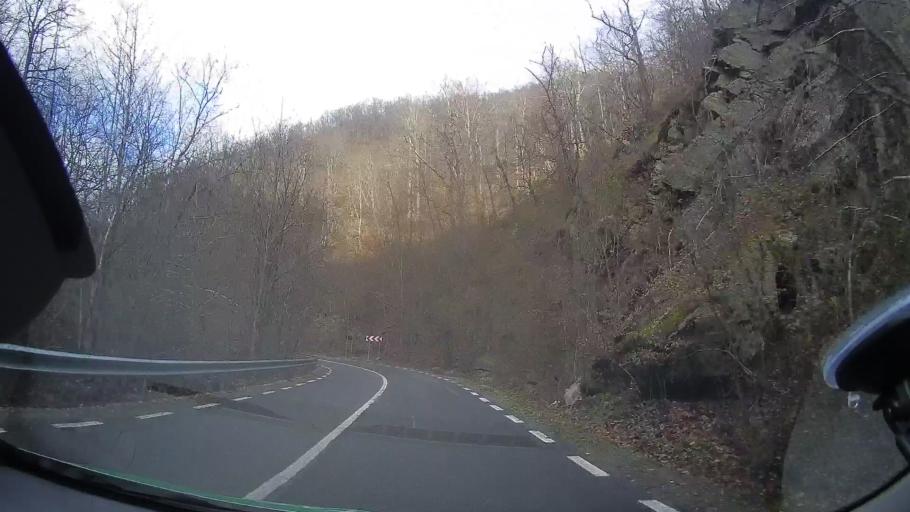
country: RO
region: Cluj
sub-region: Comuna Valea Ierii
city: Valea Ierii
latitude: 46.6263
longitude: 23.3898
